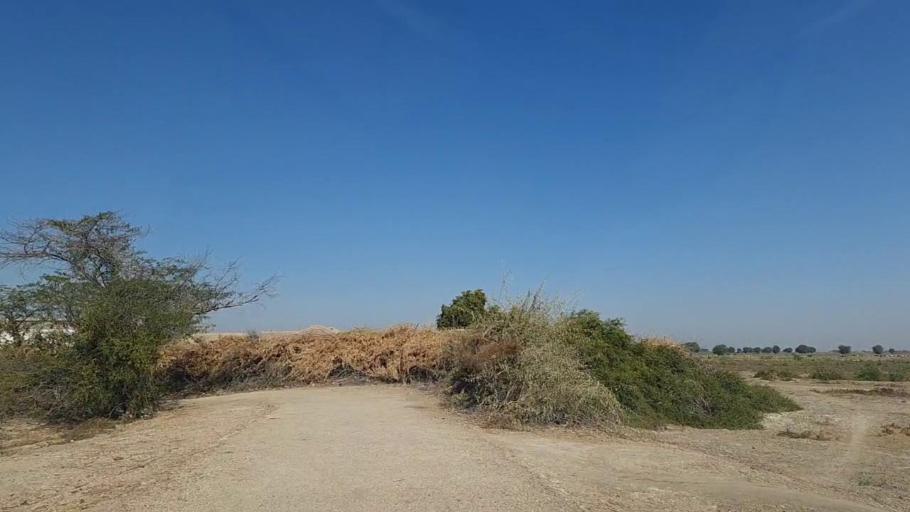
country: PK
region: Sindh
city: Kunri
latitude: 25.3003
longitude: 69.5427
